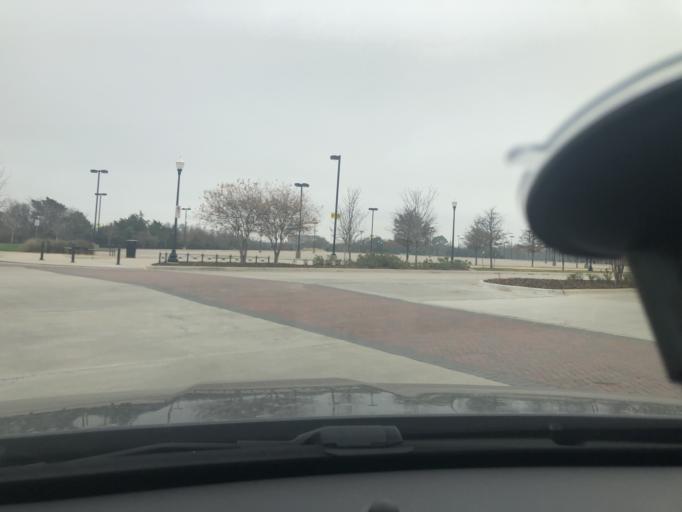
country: US
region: Texas
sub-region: Tarrant County
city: River Oaks
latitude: 32.7412
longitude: -97.3664
